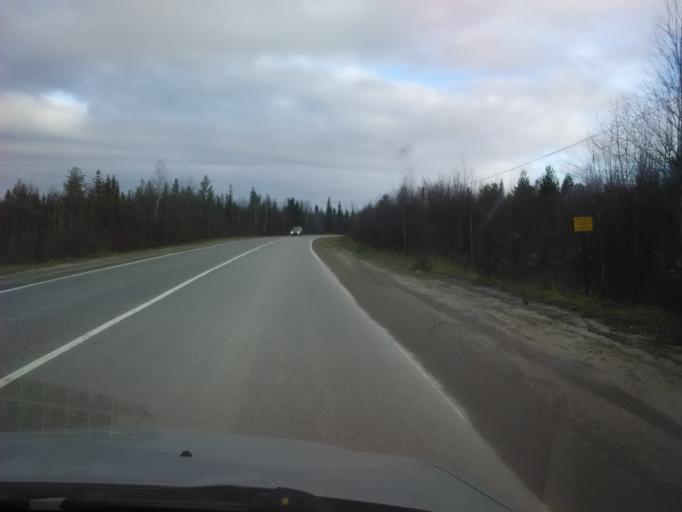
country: RU
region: Murmansk
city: Polyarnyye Zori
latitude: 67.3864
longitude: 32.5158
